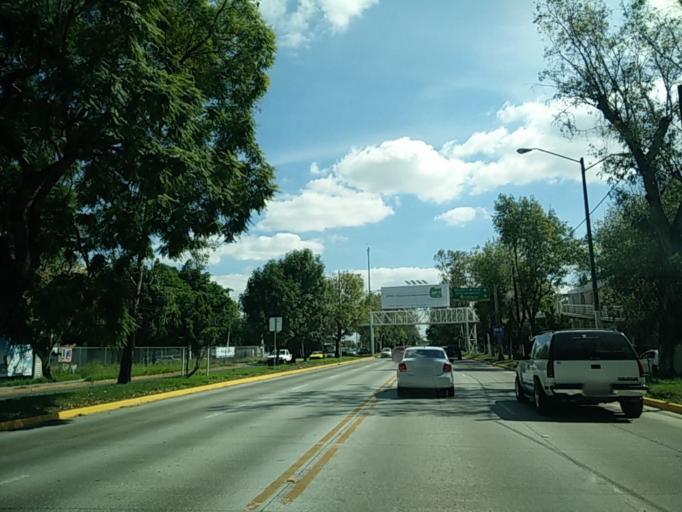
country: MX
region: Jalisco
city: Zapopan2
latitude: 20.6923
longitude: -103.4514
